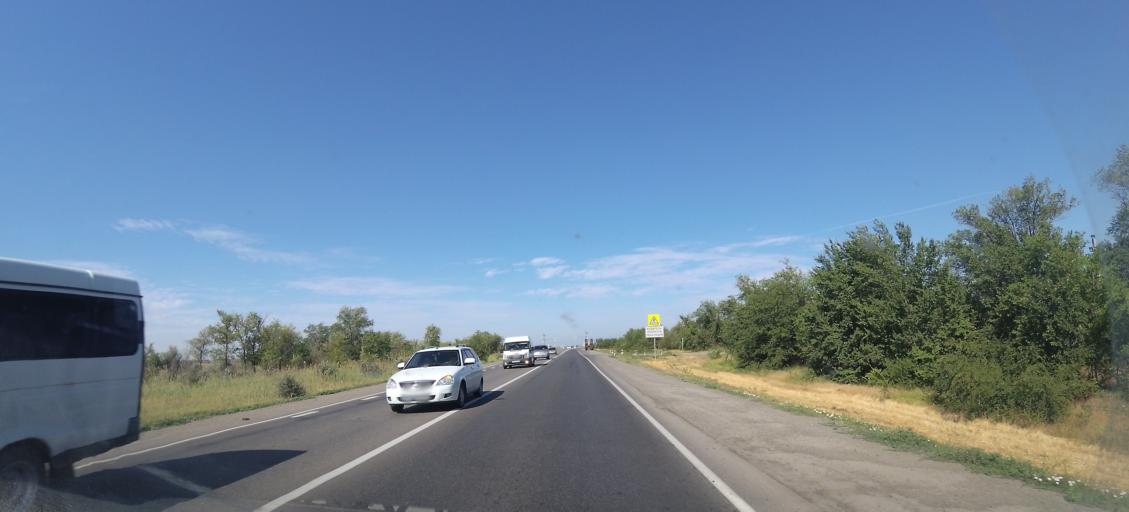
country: RU
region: Volgograd
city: Oktyabr'skiy
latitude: 48.6802
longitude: 43.9086
